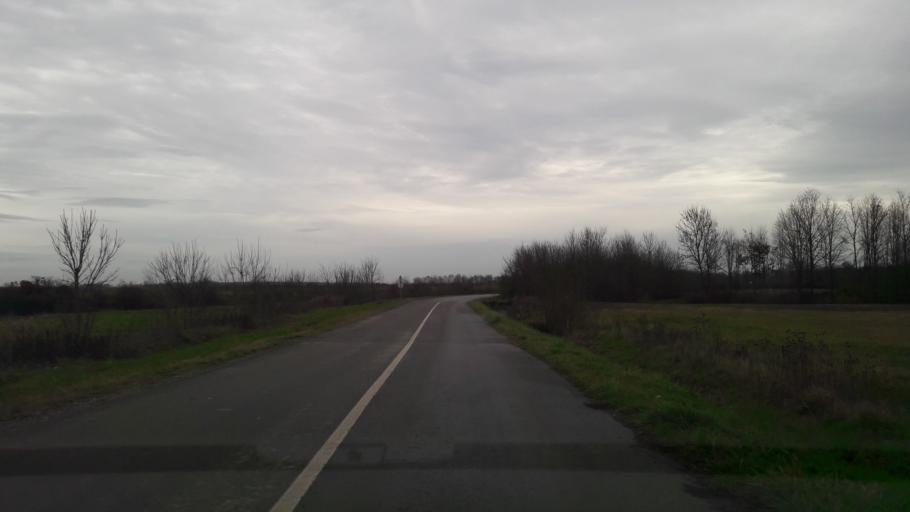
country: HR
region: Virovitick-Podravska
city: Zdenci
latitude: 45.6100
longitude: 18.0242
